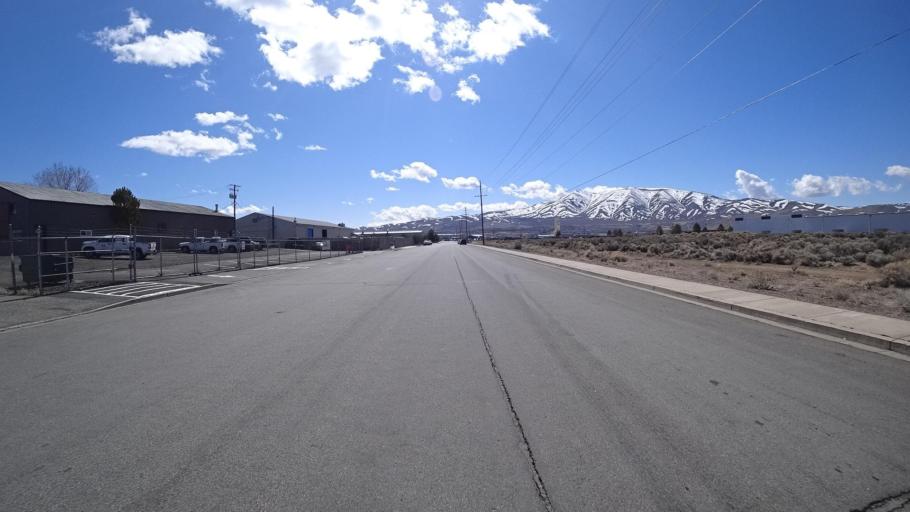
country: US
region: Nevada
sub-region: Washoe County
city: Lemmon Valley
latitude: 39.6565
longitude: -119.8862
